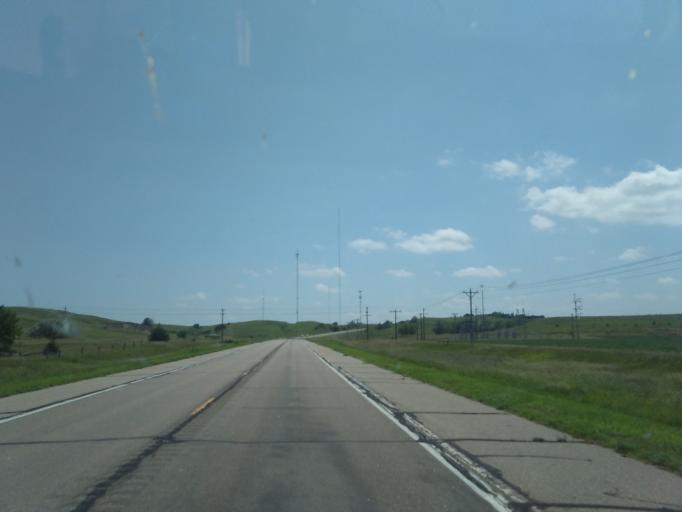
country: US
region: Nebraska
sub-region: Dawson County
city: Lexington
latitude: 40.7101
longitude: -99.7873
